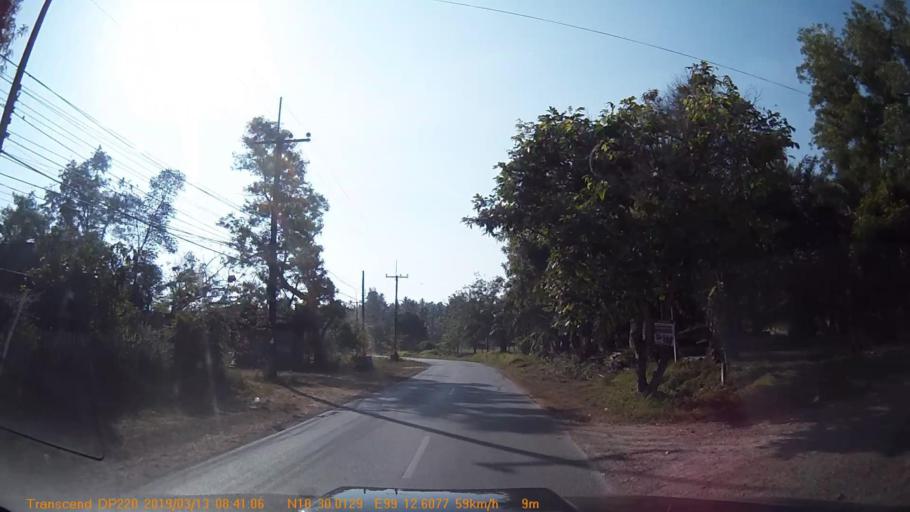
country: TH
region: Chumphon
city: Chumphon
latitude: 10.5001
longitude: 99.2102
